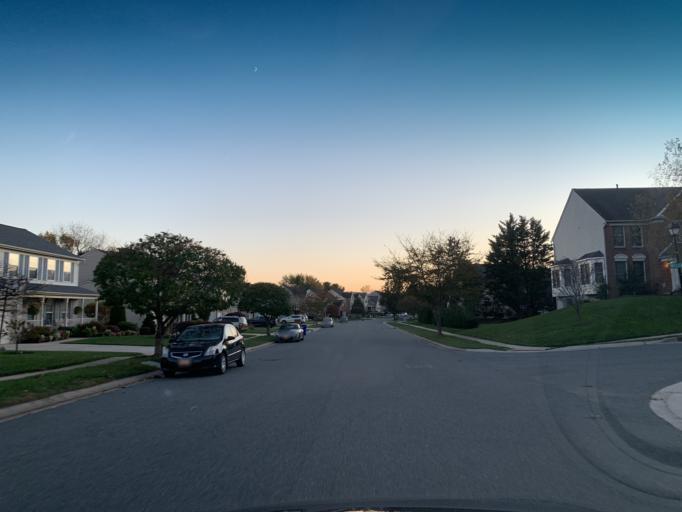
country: US
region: Maryland
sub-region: Harford County
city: Bel Air South
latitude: 39.5340
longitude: -76.3024
